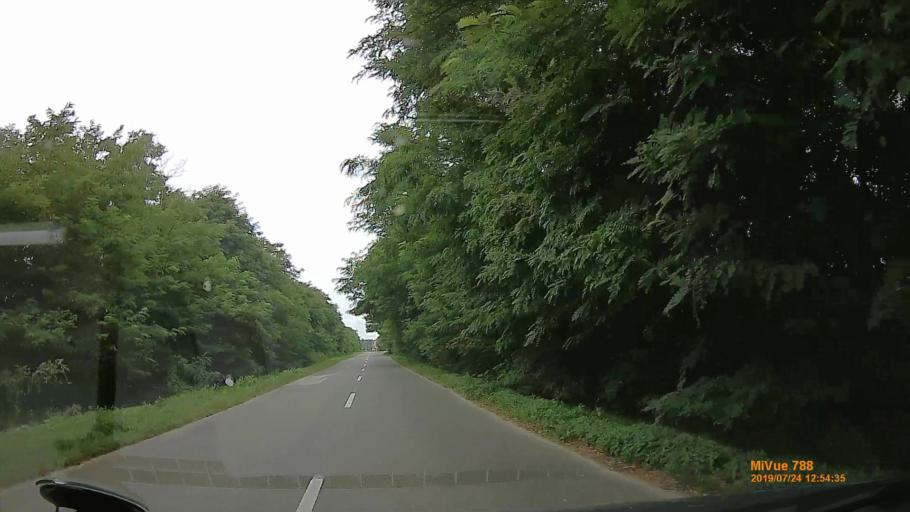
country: HU
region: Szabolcs-Szatmar-Bereg
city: Aranyosapati
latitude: 48.2172
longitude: 22.2977
